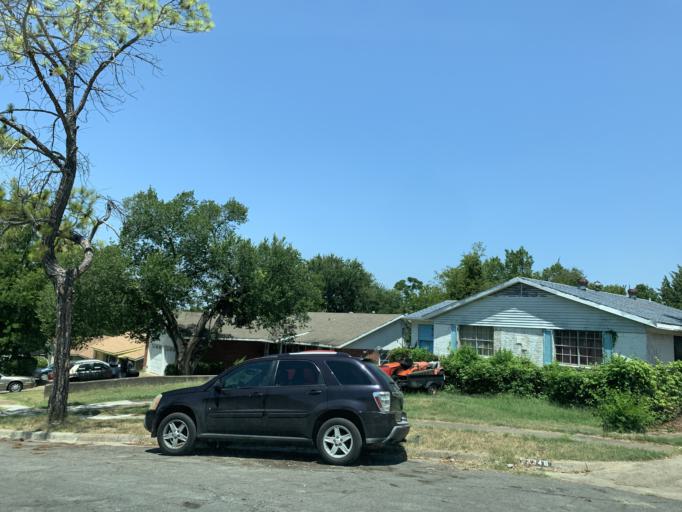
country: US
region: Texas
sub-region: Dallas County
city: Hutchins
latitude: 32.6821
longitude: -96.7639
